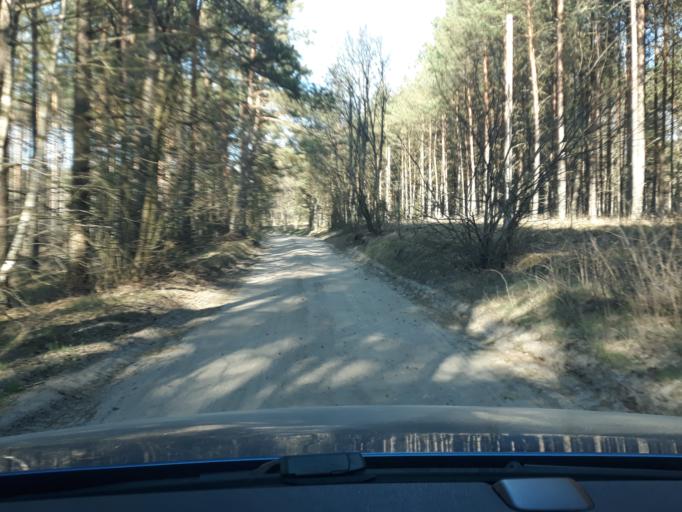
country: PL
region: Pomeranian Voivodeship
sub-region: Powiat bytowski
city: Lipnica
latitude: 53.9104
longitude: 17.4300
